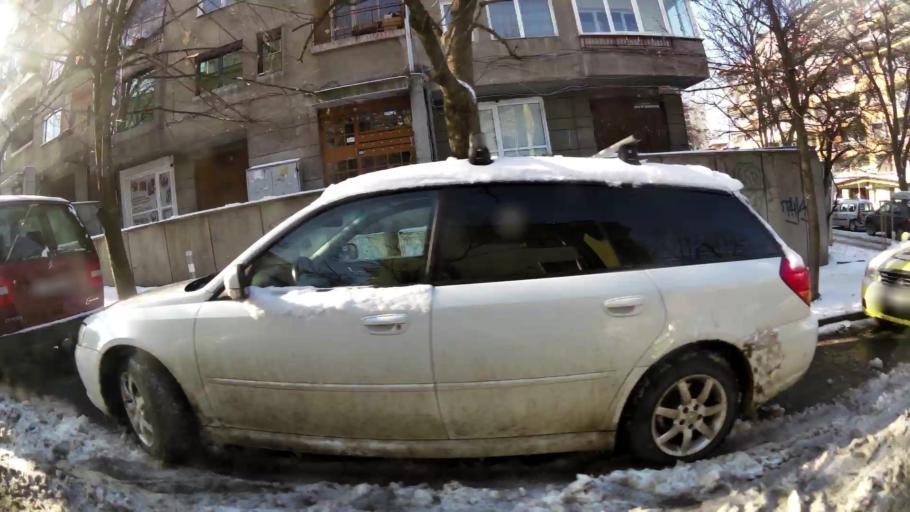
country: BG
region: Sofia-Capital
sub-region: Stolichna Obshtina
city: Sofia
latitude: 42.6781
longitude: 23.3325
